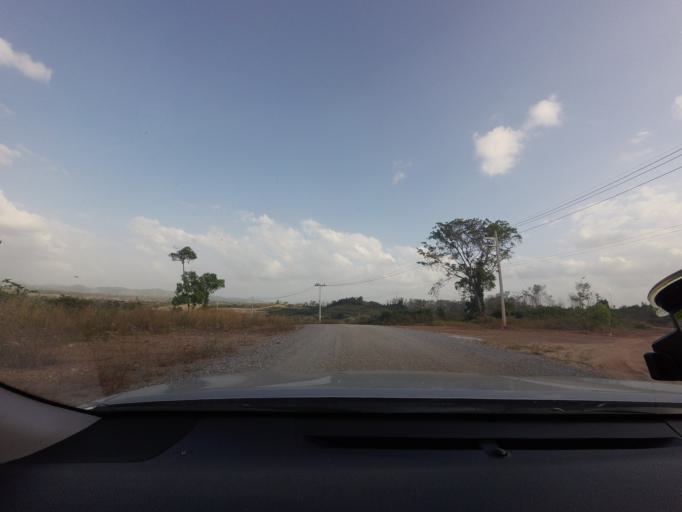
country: TH
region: Pattani
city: Mae Lan
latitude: 6.6050
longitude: 101.2477
